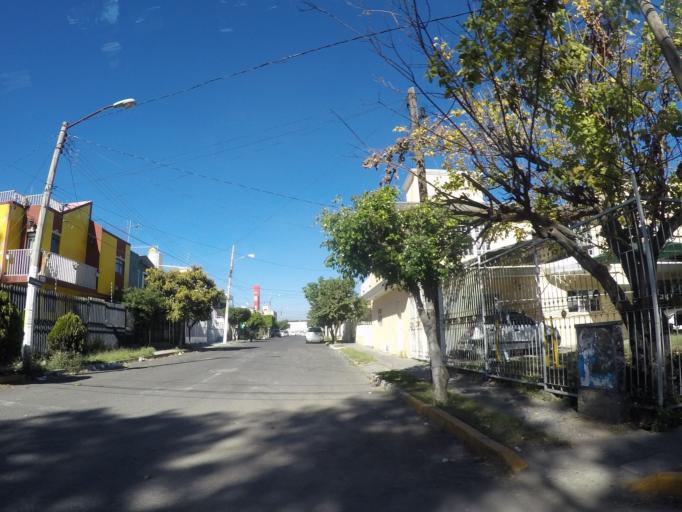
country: MX
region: Jalisco
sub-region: Zapopan
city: Zapopan
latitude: 20.7305
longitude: -103.3497
